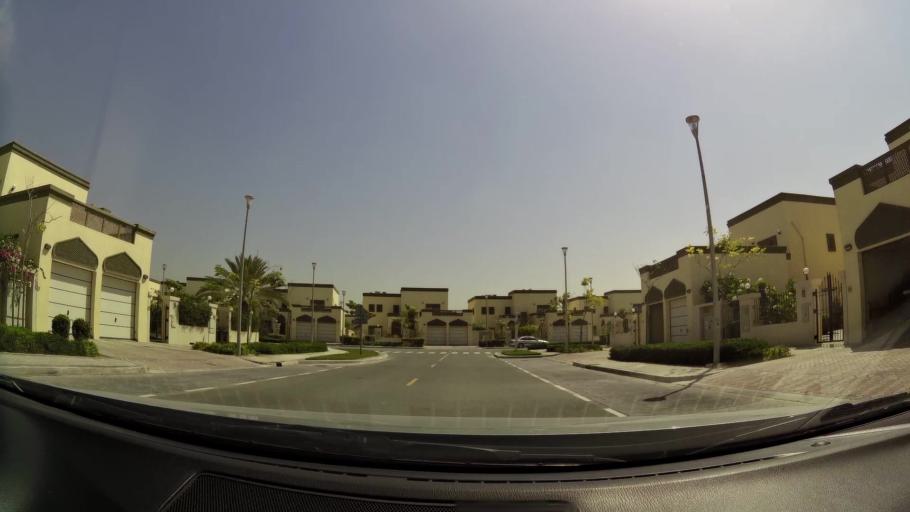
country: AE
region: Dubai
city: Dubai
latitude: 25.0452
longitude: 55.1551
